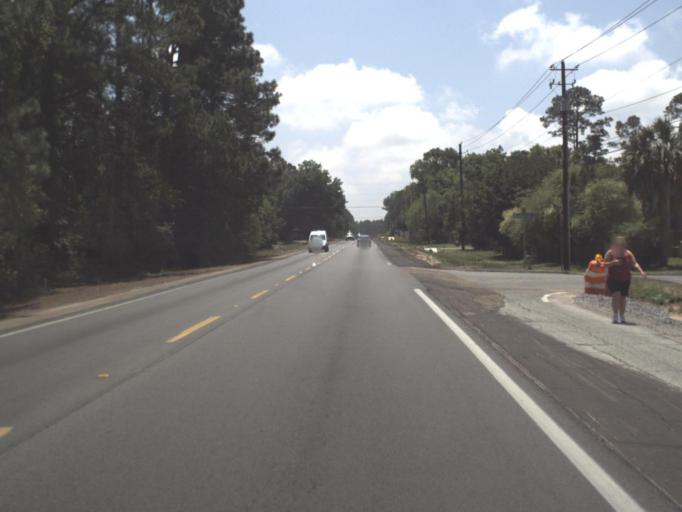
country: US
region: Florida
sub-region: Escambia County
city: Myrtle Grove
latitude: 30.4100
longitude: -87.3176
